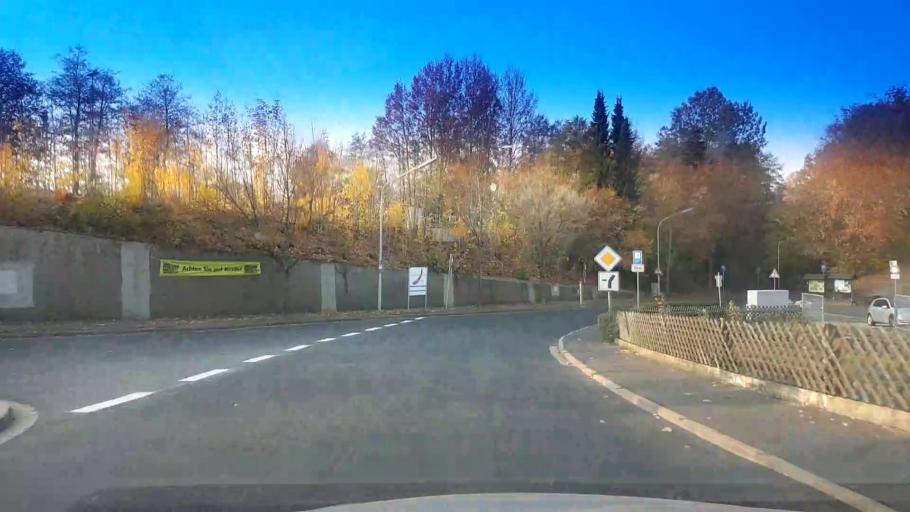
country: DE
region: Bavaria
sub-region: Upper Franconia
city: Schirnding
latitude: 50.0787
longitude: 12.2303
